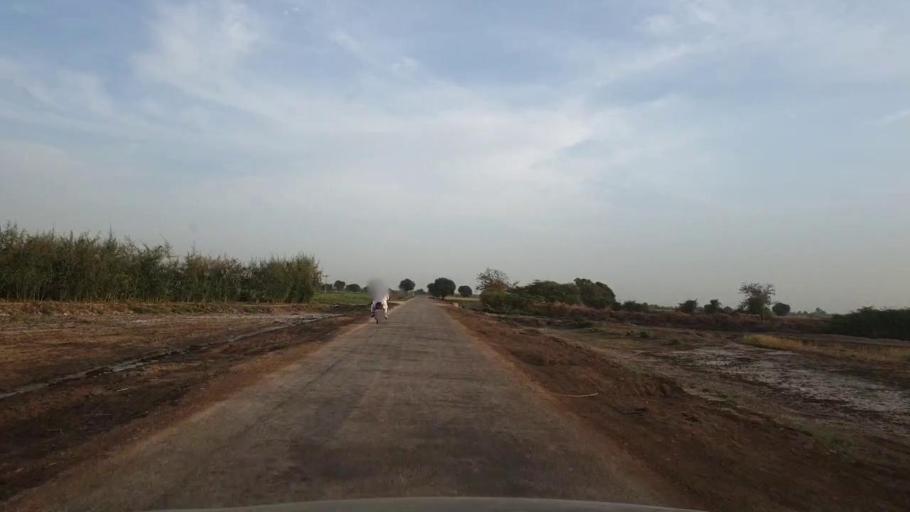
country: PK
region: Sindh
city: Kunri
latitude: 25.1667
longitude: 69.5462
